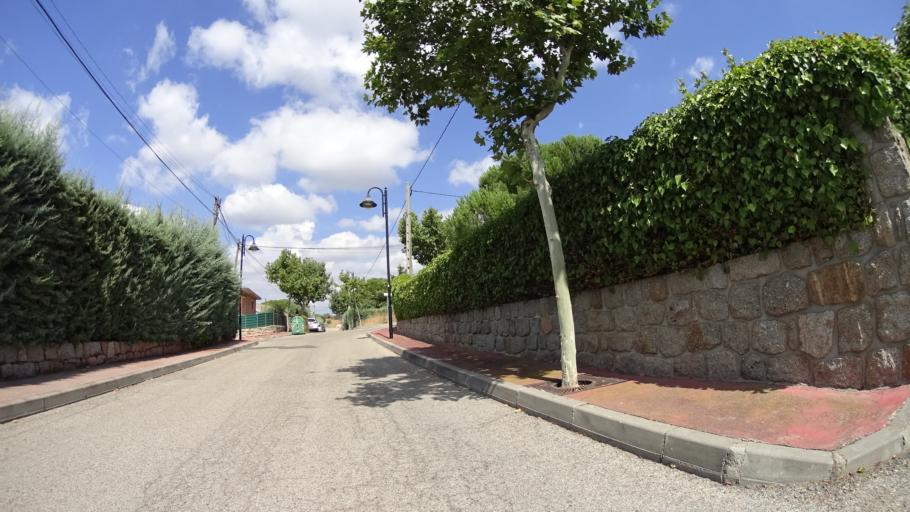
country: ES
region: Madrid
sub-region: Provincia de Madrid
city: Galapagar
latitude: 40.5867
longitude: -3.9978
